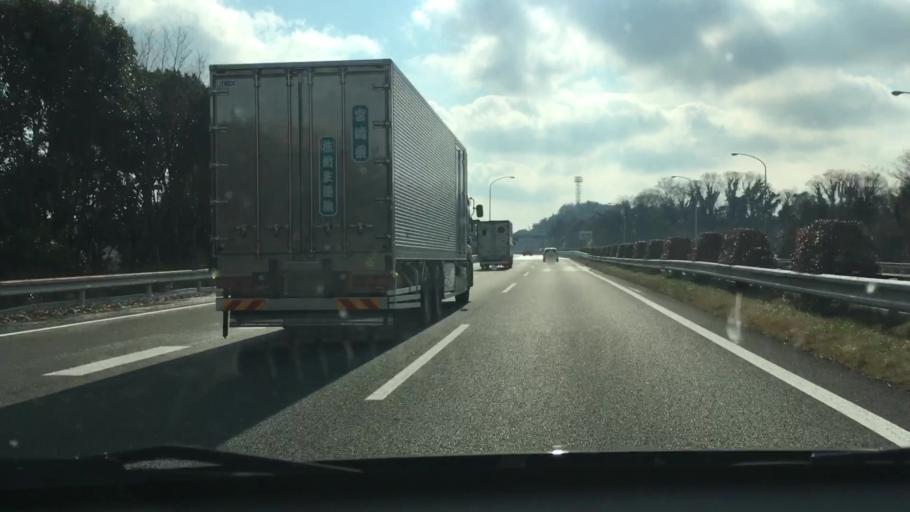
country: JP
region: Kumamoto
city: Kumamoto
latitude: 32.7322
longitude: 130.7760
